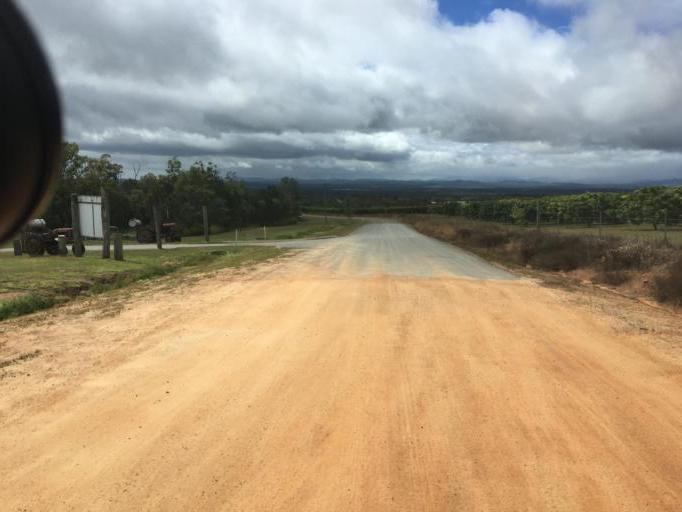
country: AU
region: Queensland
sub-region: Tablelands
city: Mareeba
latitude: -17.0113
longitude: 145.3380
